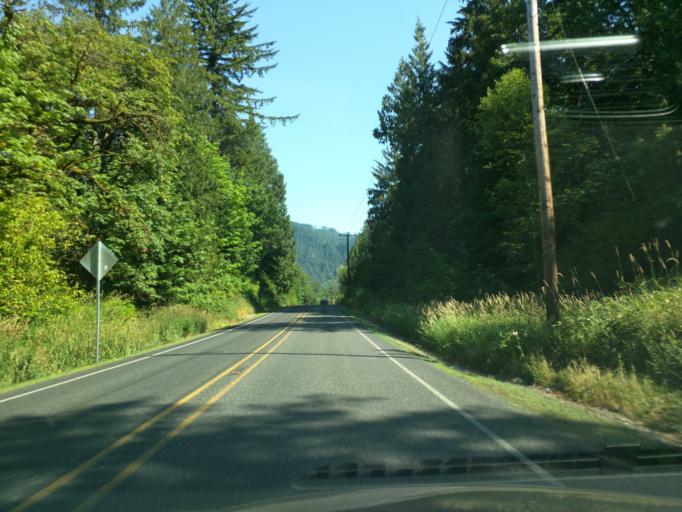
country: US
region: Washington
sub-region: Whatcom County
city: Peaceful Valley
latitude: 48.7996
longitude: -122.1945
